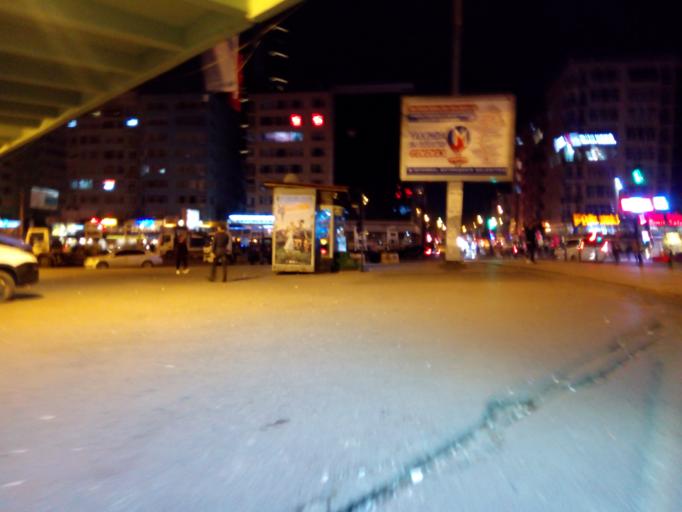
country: TR
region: Istanbul
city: Sisli
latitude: 41.0901
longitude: 29.0006
